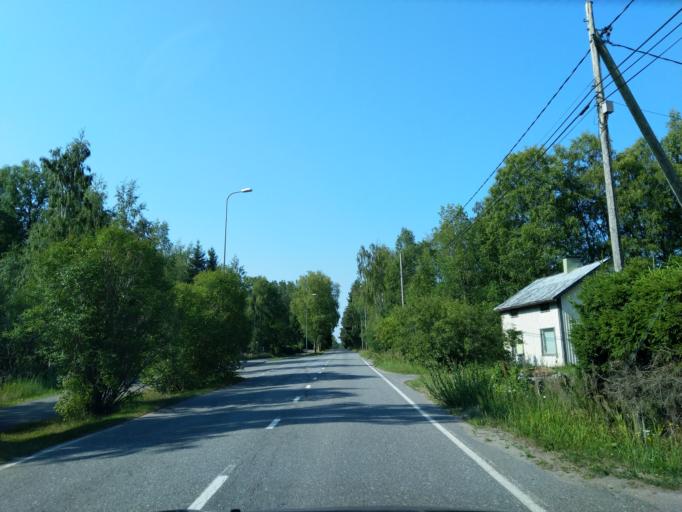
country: FI
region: Satakunta
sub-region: Pori
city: Pomarkku
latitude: 61.7047
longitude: 22.0251
